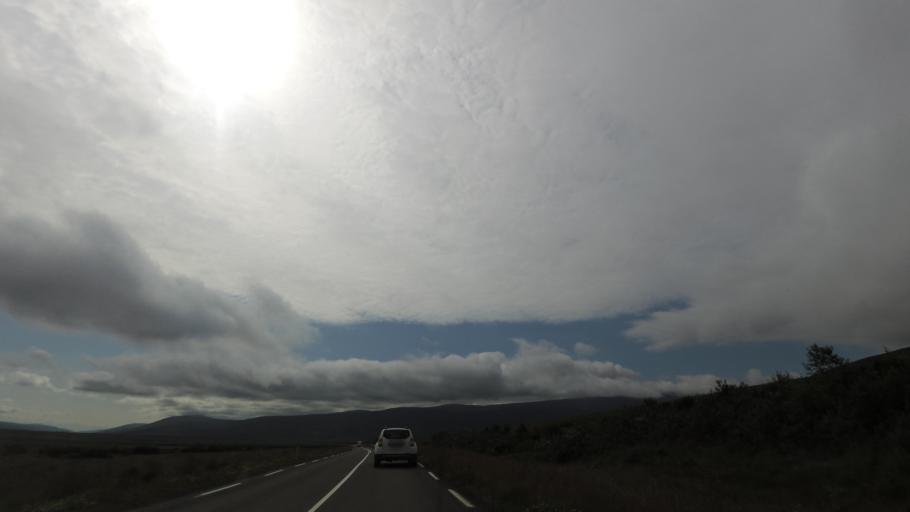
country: IS
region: Northeast
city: Laugar
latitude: 65.7238
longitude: -17.5971
